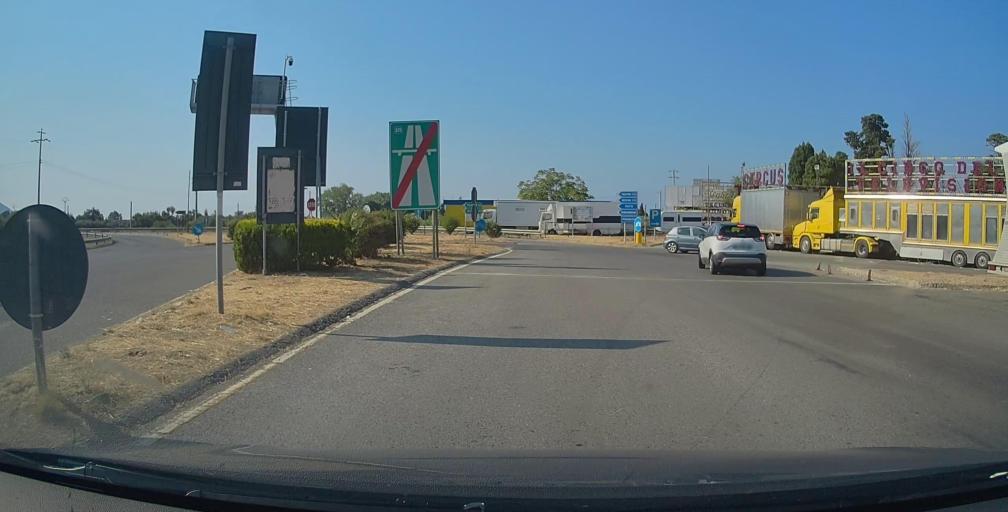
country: IT
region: Sicily
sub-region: Messina
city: Patti
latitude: 38.1457
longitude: 14.9991
